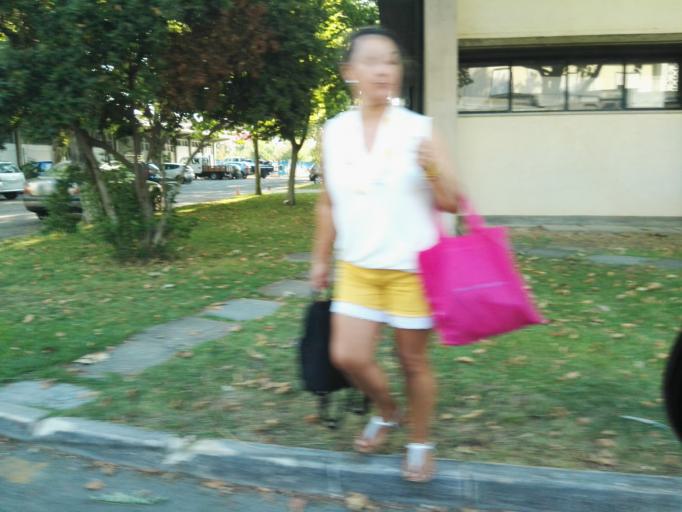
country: PT
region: Lisbon
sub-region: Odivelas
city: Olival do Basto
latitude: 38.7588
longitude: -9.1428
